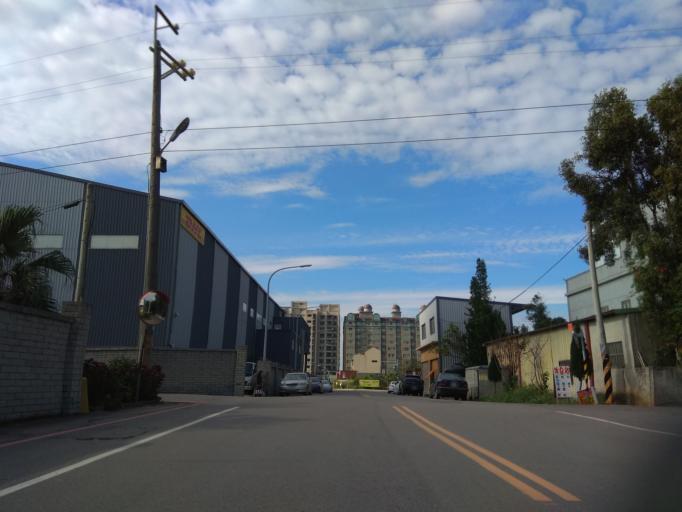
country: TW
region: Taiwan
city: Taoyuan City
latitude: 25.0493
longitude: 121.1768
